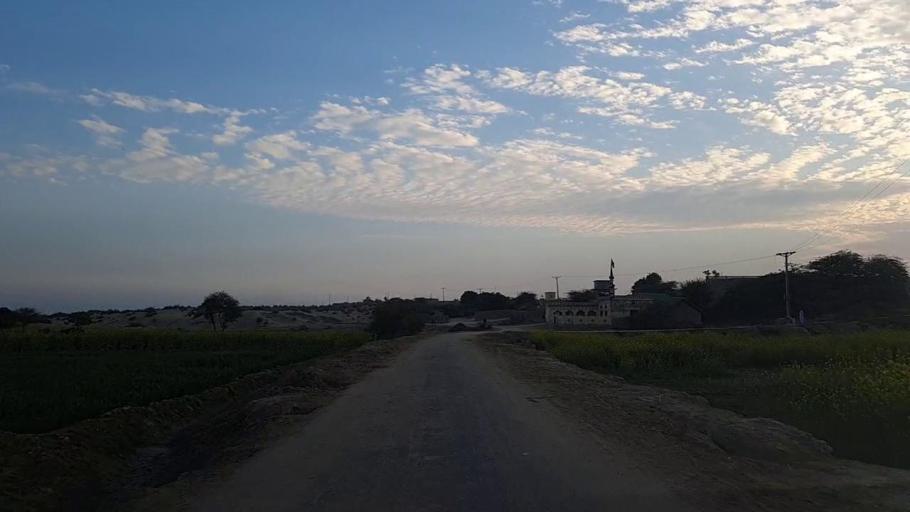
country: PK
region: Sindh
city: Daur
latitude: 26.4134
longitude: 68.4678
